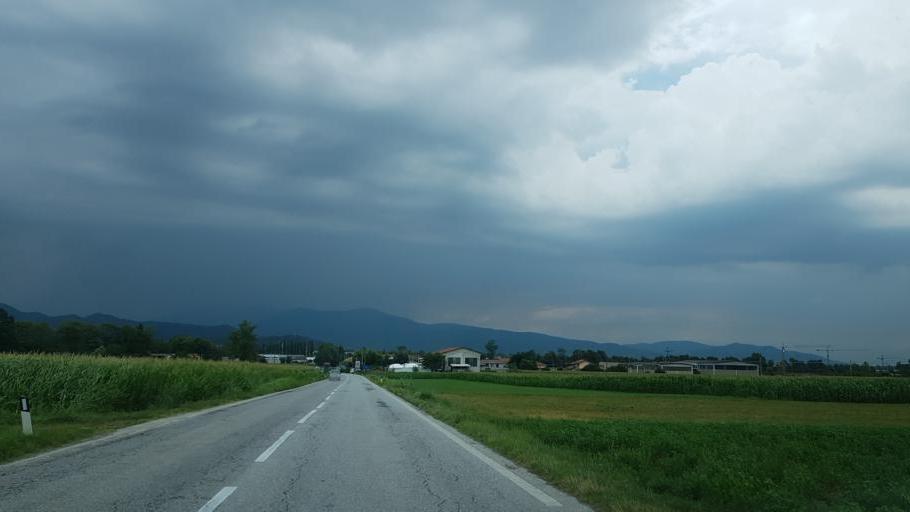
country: IT
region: Piedmont
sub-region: Provincia di Cuneo
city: Cervasca
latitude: 44.3877
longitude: 7.4618
